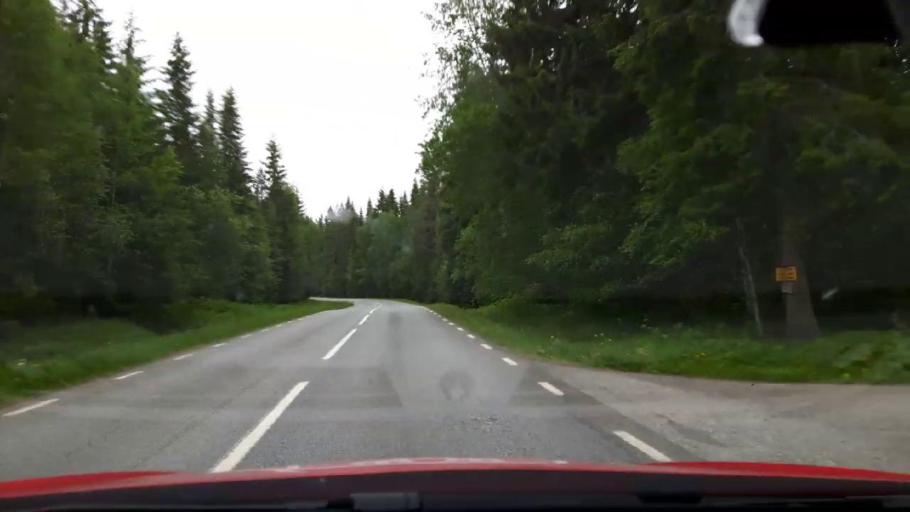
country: SE
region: Jaemtland
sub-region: Stroemsunds Kommun
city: Stroemsund
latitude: 63.4545
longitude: 15.4621
